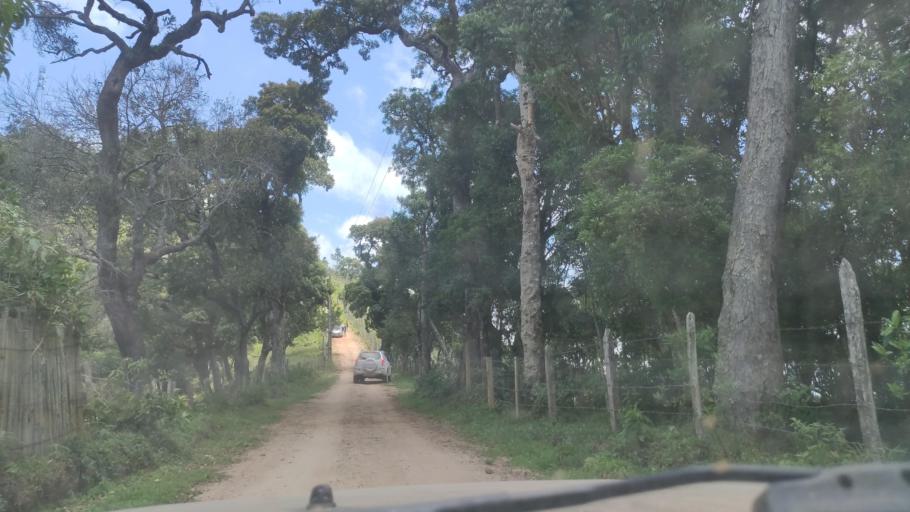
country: BR
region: Minas Gerais
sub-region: Cambui
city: Cambui
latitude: -22.6863
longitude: -45.9573
